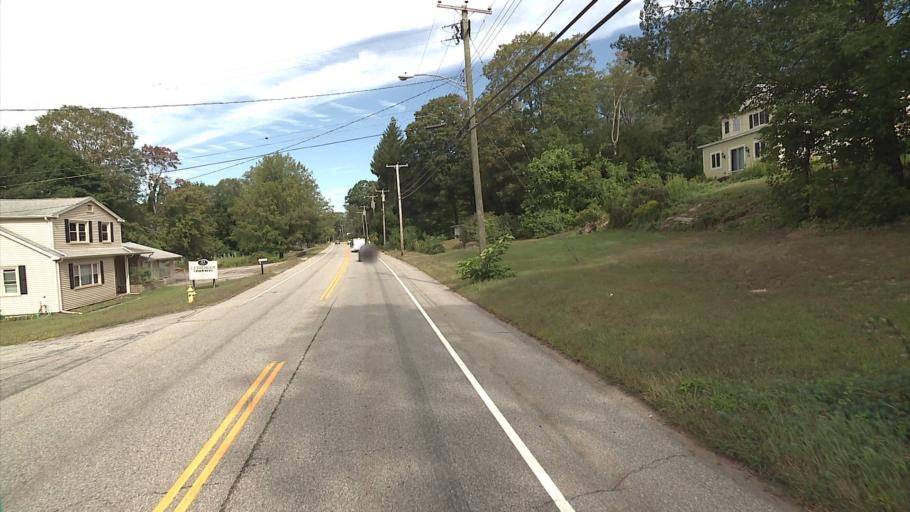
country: US
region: Connecticut
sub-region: Tolland County
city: Mansfield City
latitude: 41.7295
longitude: -72.2462
